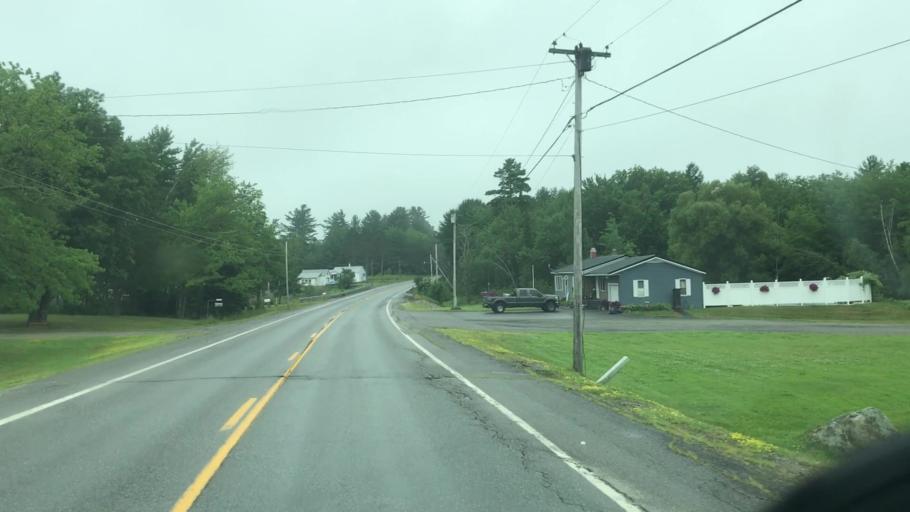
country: US
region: Maine
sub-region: Penobscot County
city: Howland
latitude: 45.2884
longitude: -68.6239
